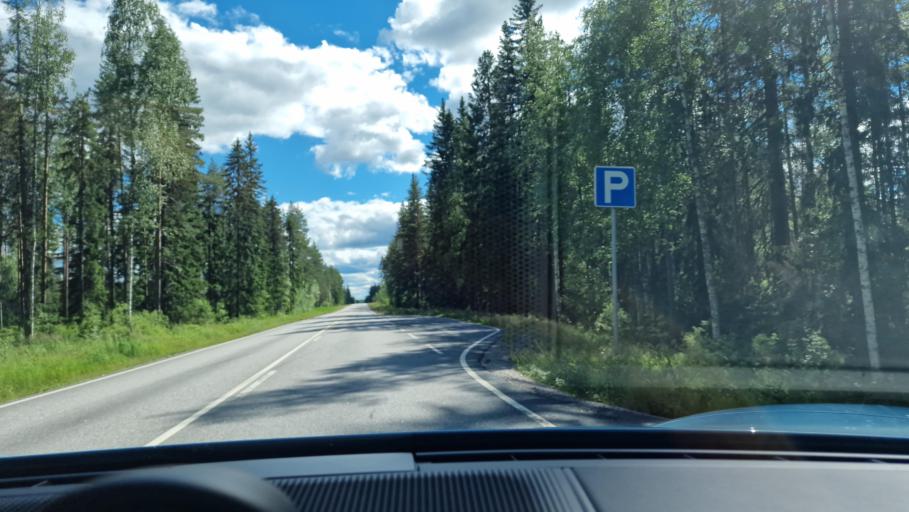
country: FI
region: Central Finland
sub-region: Saarijaervi-Viitasaari
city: Pylkoenmaeki
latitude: 62.6440
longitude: 24.5755
